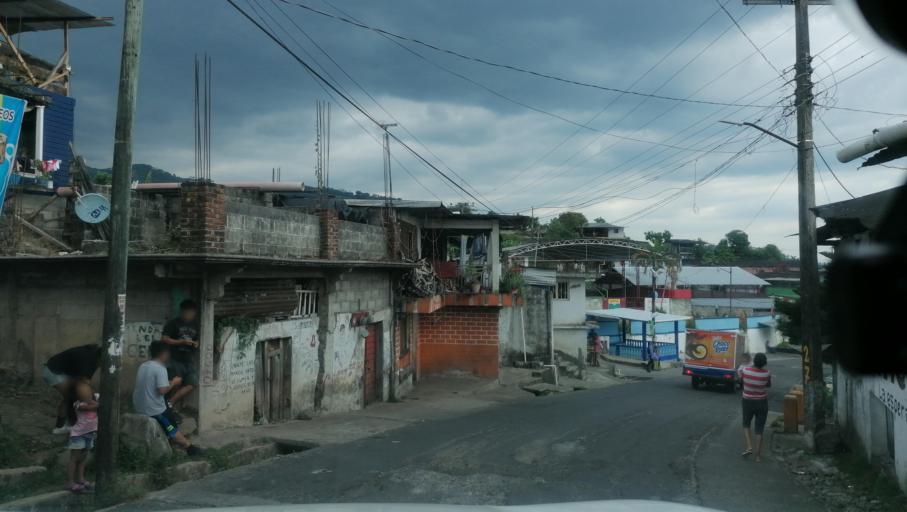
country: MX
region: Chiapas
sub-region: Cacahoatan
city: Benito Juarez
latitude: 15.0758
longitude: -92.1992
